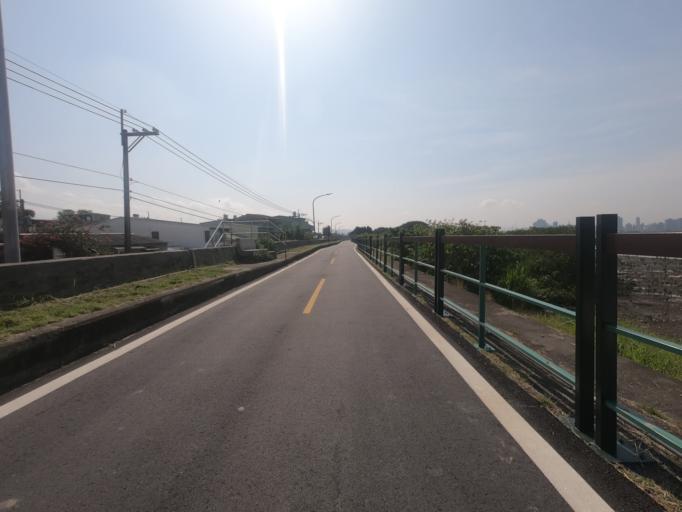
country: TW
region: Taipei
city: Taipei
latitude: 25.1060
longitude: 121.4734
